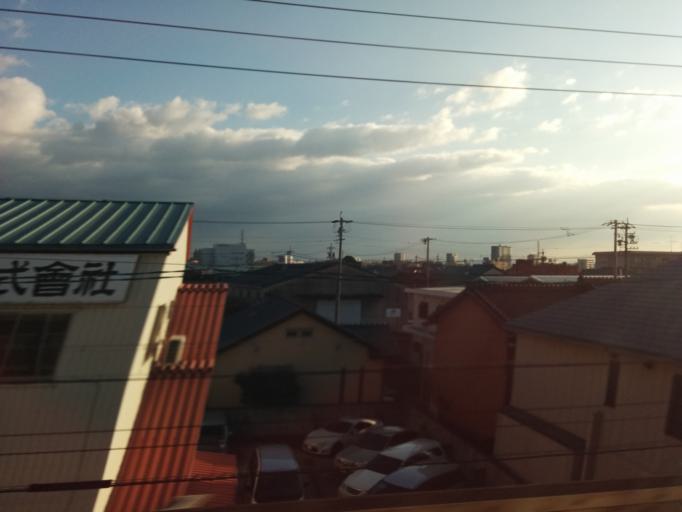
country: JP
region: Aichi
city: Obu
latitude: 35.0797
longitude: 136.9348
